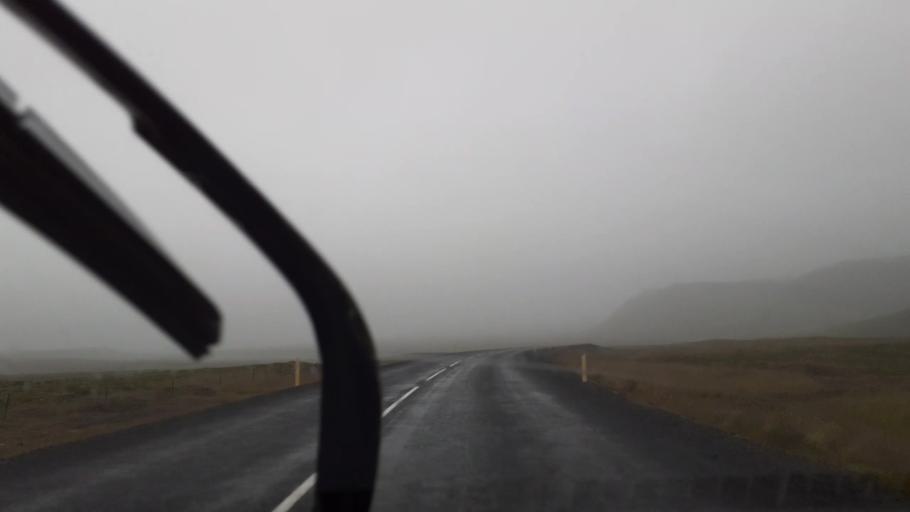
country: IS
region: Northeast
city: Husavik
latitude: 66.3826
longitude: -15.9443
